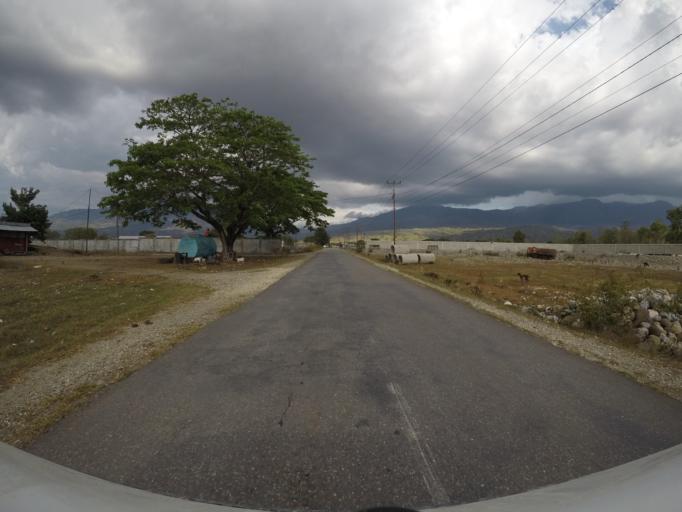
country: TL
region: Bobonaro
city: Maliana
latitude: -8.9917
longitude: 125.1867
